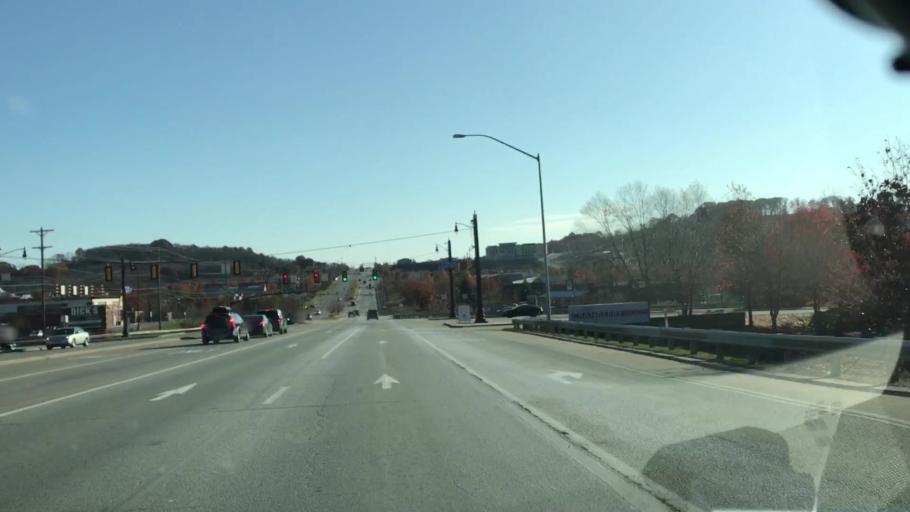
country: US
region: Pennsylvania
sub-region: Butler County
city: Fox Run
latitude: 40.6855
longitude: -80.0886
